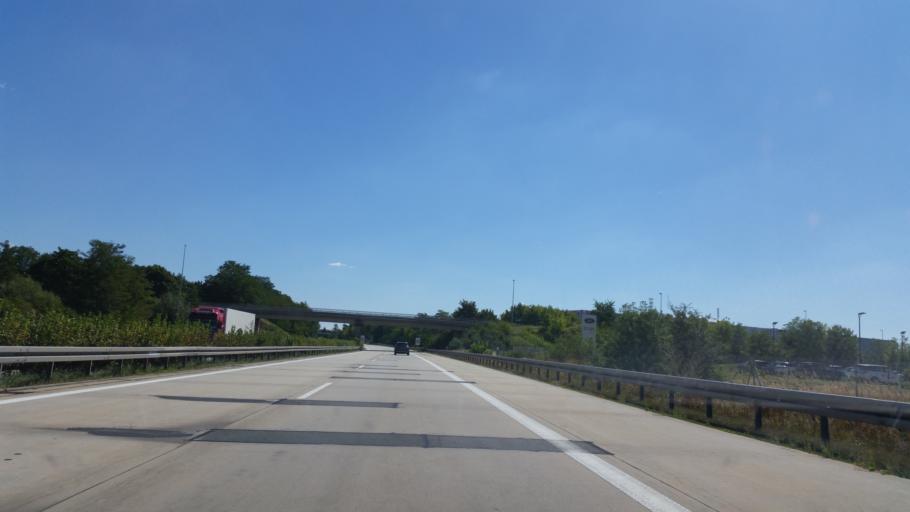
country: DE
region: Brandenburg
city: Cottbus
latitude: 51.7203
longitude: 14.3162
